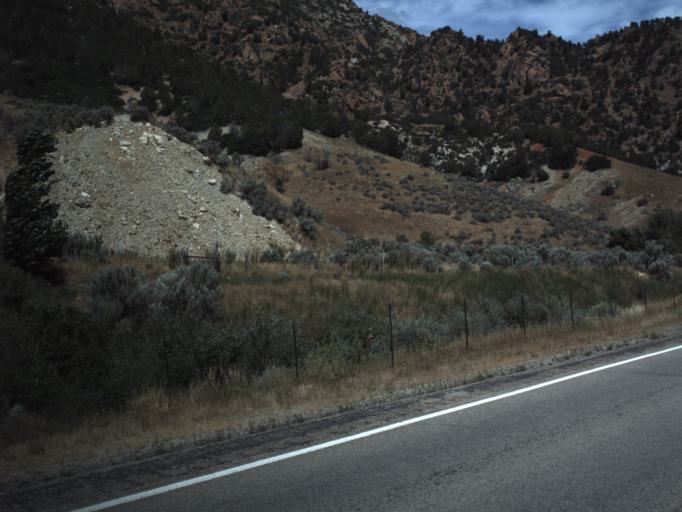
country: US
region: Utah
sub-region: Utah County
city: Woodland Hills
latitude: 39.9831
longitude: -111.5024
